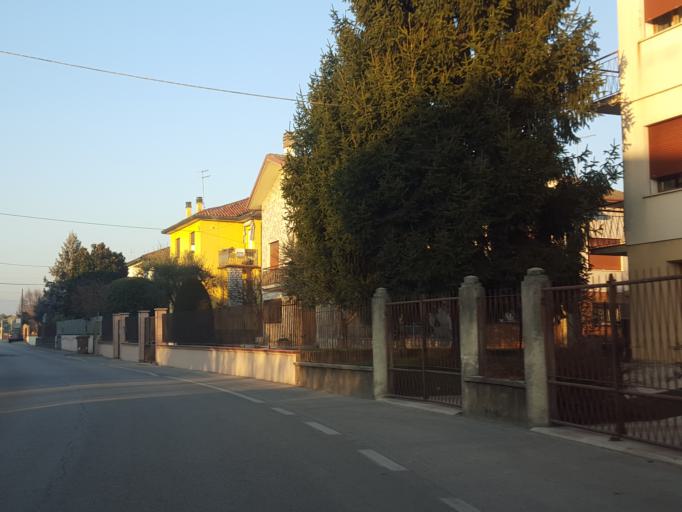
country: IT
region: Veneto
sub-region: Provincia di Vicenza
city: Villaggio Montegrappa
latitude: 45.5445
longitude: 11.6062
